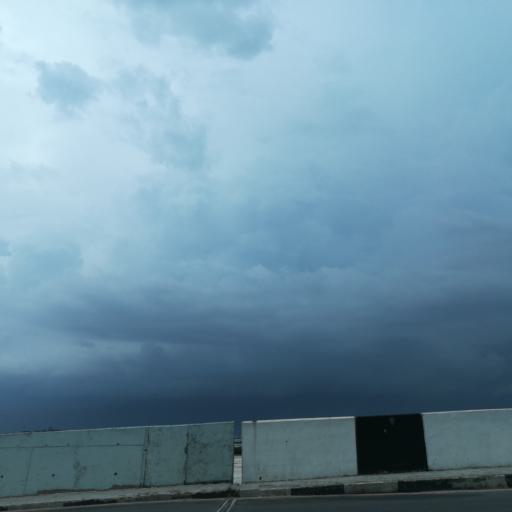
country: NG
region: Rivers
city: Port Harcourt
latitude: 4.8066
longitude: 7.0604
